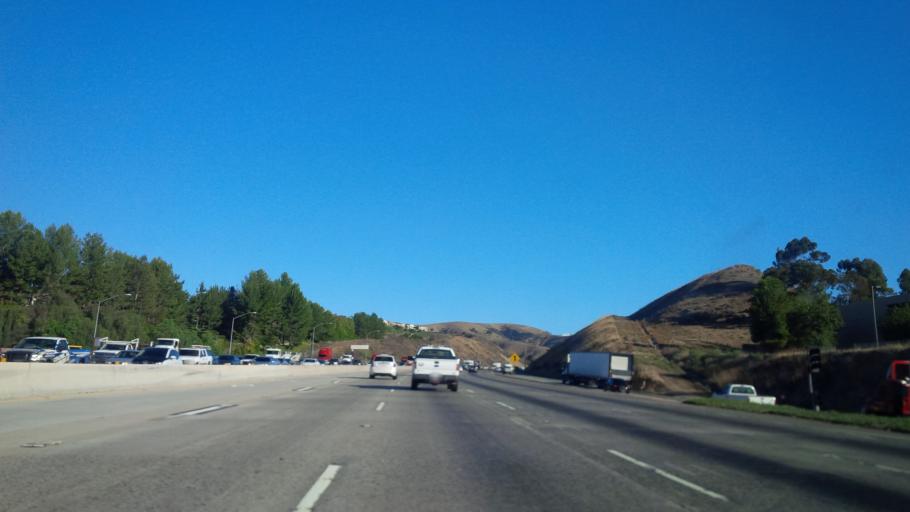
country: US
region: California
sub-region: Orange County
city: Brea
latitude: 33.9277
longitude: -117.8801
